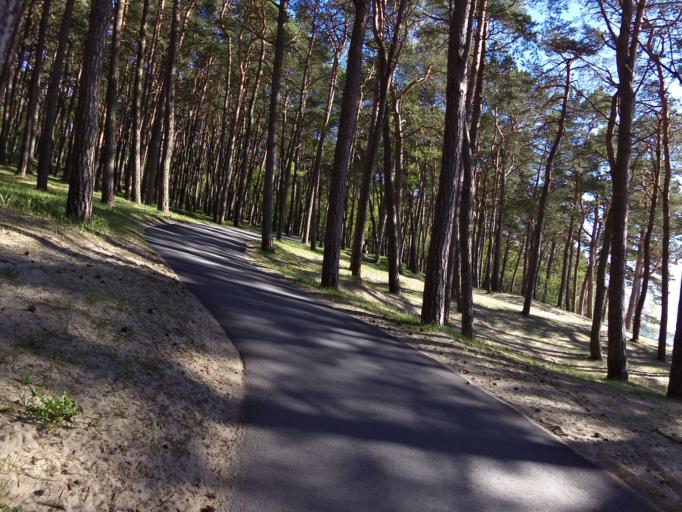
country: EE
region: Harju
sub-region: Viimsi vald
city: Viimsi
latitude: 59.4826
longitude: 24.8381
